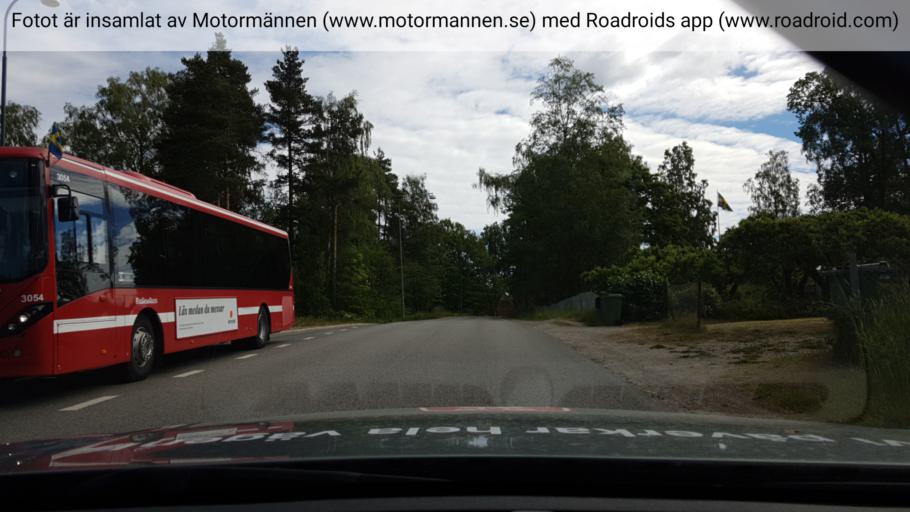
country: SE
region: Stockholm
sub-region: Nynashamns Kommun
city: Osmo
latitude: 58.9825
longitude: 17.8970
